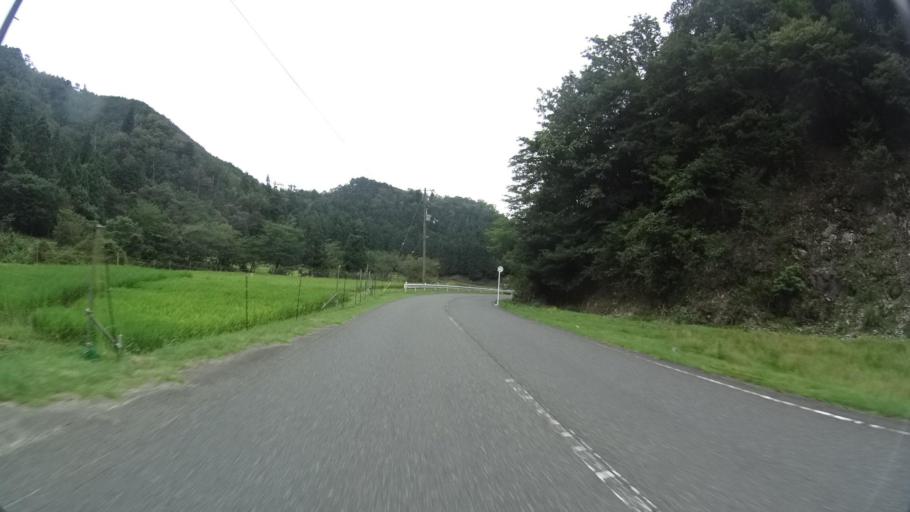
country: JP
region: Kyoto
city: Miyazu
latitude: 35.4641
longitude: 135.1534
